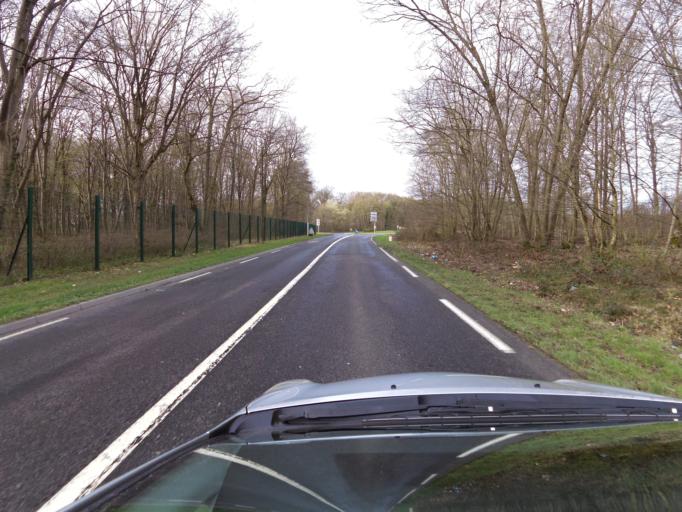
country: FR
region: Picardie
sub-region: Departement de l'Oise
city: Ver-sur-Launette
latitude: 49.1261
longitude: 2.6868
